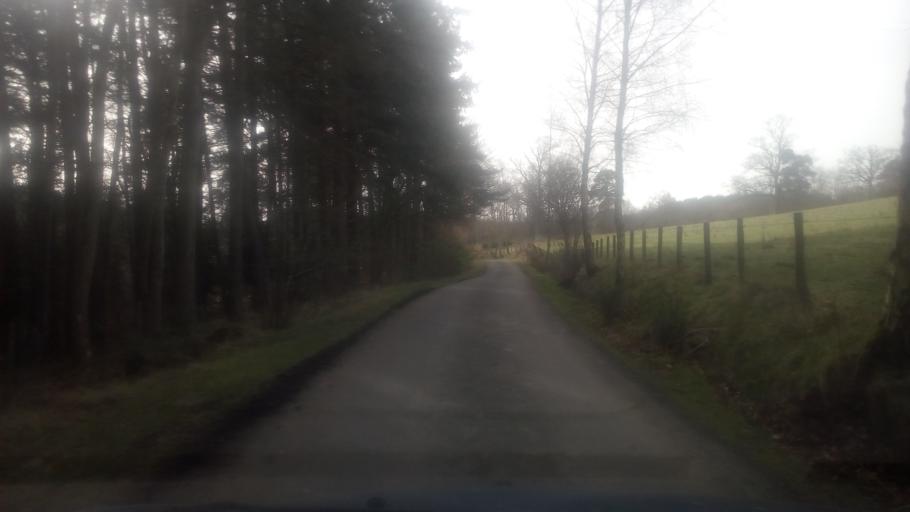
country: GB
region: Scotland
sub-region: The Scottish Borders
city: Jedburgh
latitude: 55.4393
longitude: -2.6405
